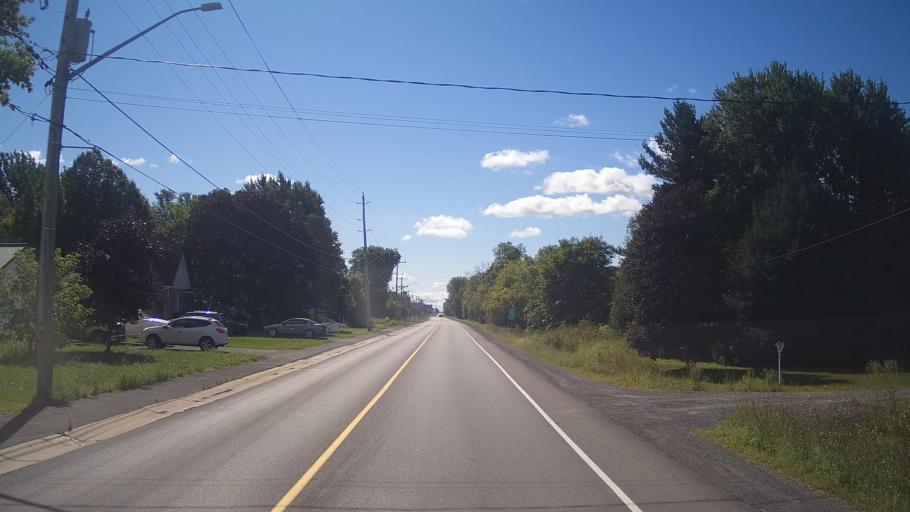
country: US
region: New York
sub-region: St. Lawrence County
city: Norfolk
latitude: 44.9719
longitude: -75.2414
